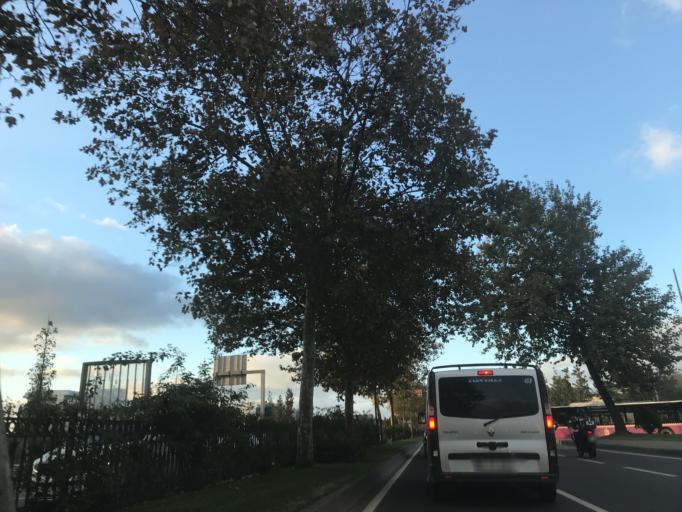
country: TR
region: Istanbul
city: Sisli
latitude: 41.1146
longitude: 29.0247
